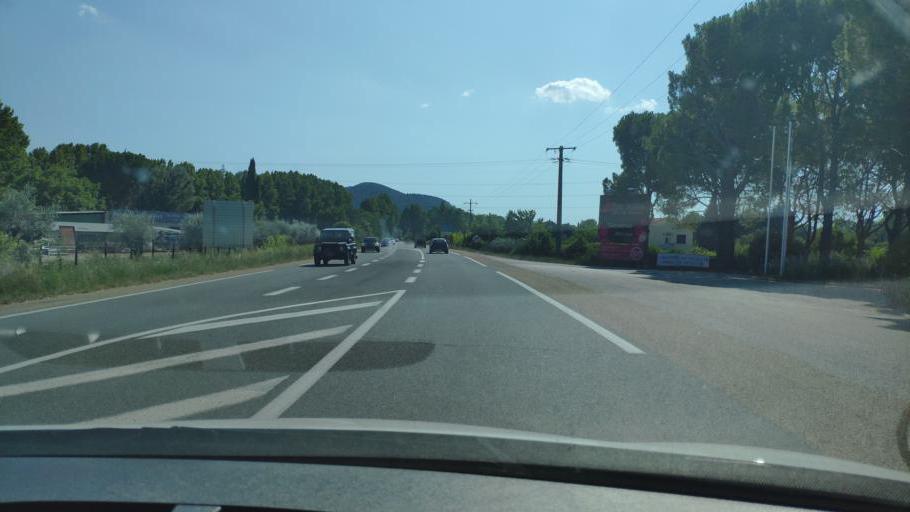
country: FR
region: Provence-Alpes-Cote d'Azur
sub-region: Departement du Var
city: Les Arcs
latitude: 43.4461
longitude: 6.4707
